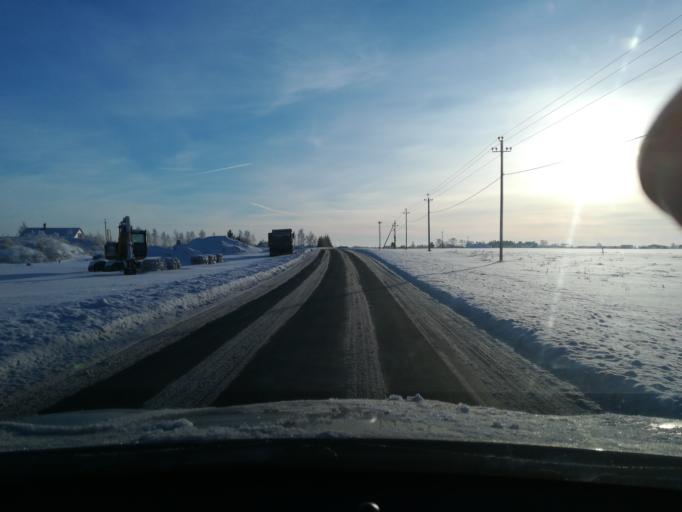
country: EE
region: Harju
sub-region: Saue linn
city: Saue
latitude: 59.3507
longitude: 24.5576
